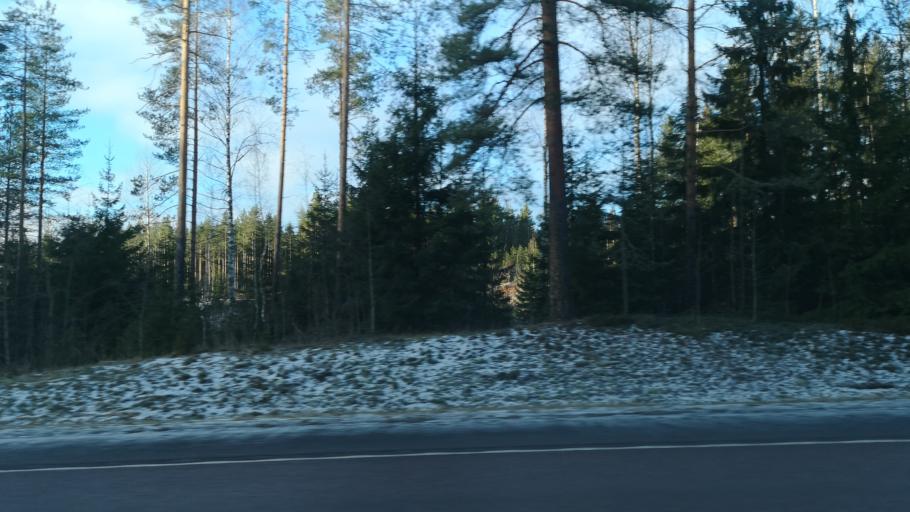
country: FI
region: Paijanne Tavastia
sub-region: Lahti
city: Heinola
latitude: 61.3286
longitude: 26.1602
